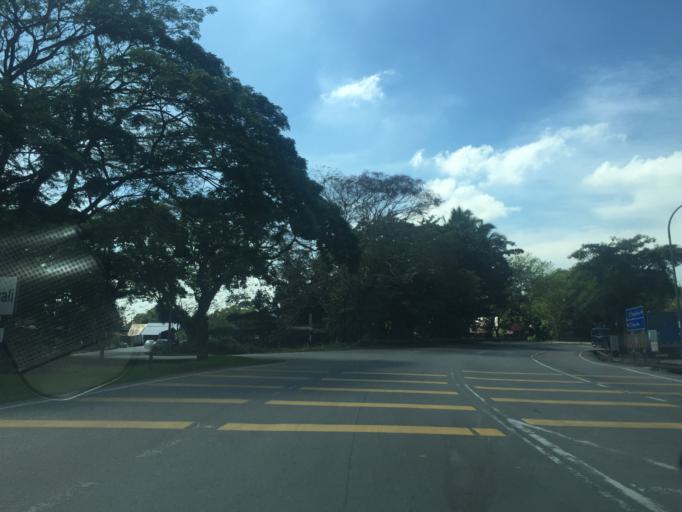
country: MY
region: Penang
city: Tasek Glugor
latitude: 5.4793
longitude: 100.5044
